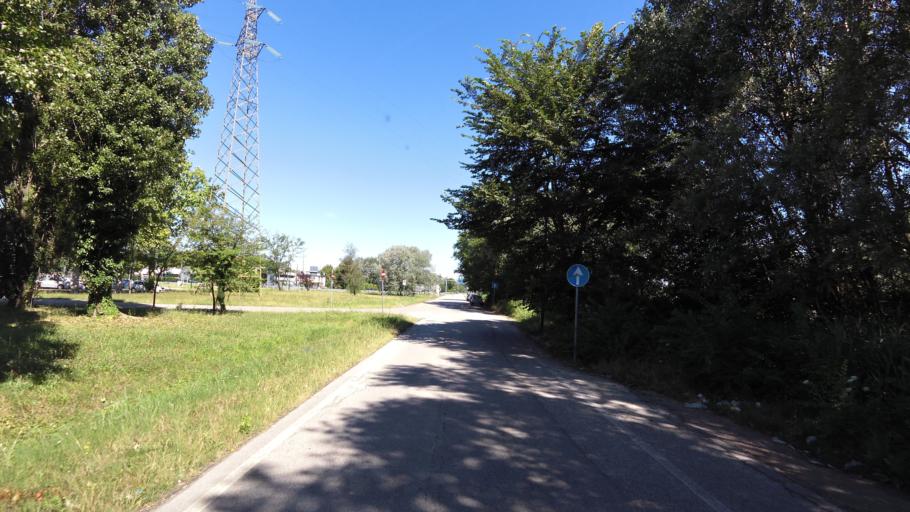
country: IT
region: Veneto
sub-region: Provincia di Venezia
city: Campalto
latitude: 45.4712
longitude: 12.2712
